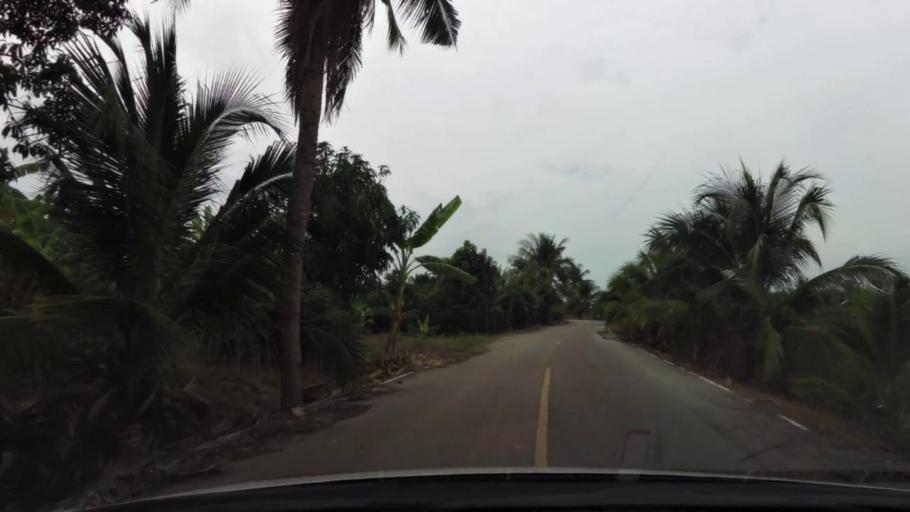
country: TH
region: Samut Sakhon
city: Ban Phaeo
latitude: 13.5880
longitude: 100.0355
